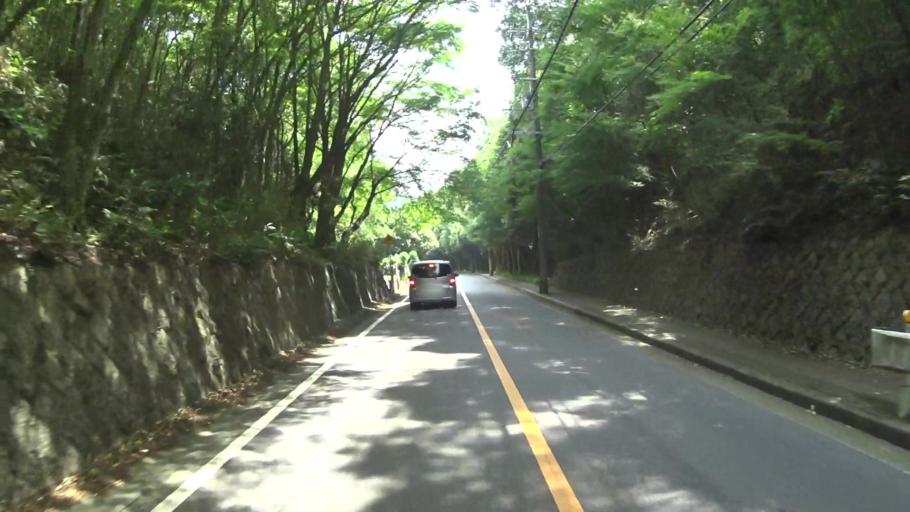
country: JP
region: Kyoto
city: Kyoto
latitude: 35.0318
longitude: 135.6958
